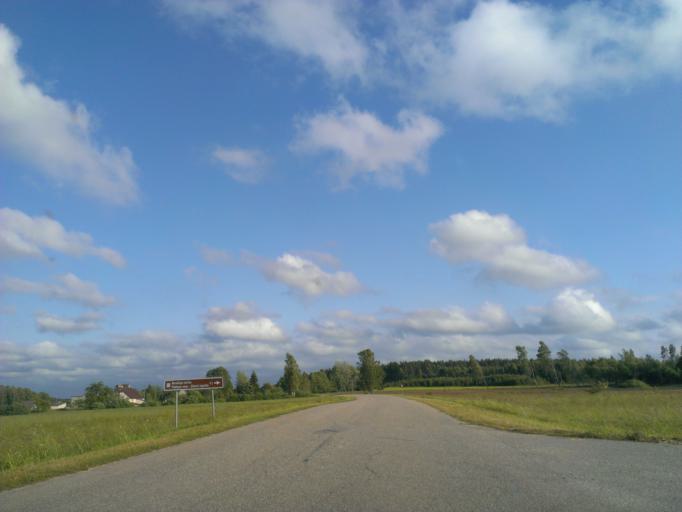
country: LV
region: Aizpute
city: Aizpute
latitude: 56.7771
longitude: 21.5199
